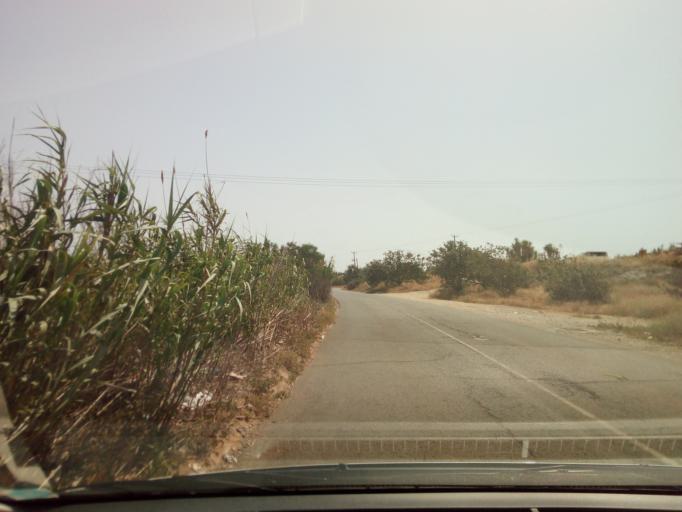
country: CY
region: Larnaka
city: Xylotymbou
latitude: 34.9879
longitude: 33.7911
